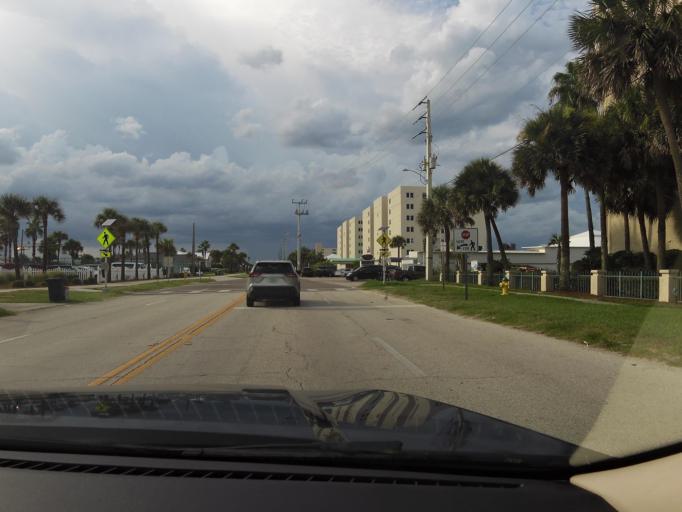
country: US
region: Florida
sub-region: Volusia County
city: Ponce Inlet
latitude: 29.1083
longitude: -80.9435
